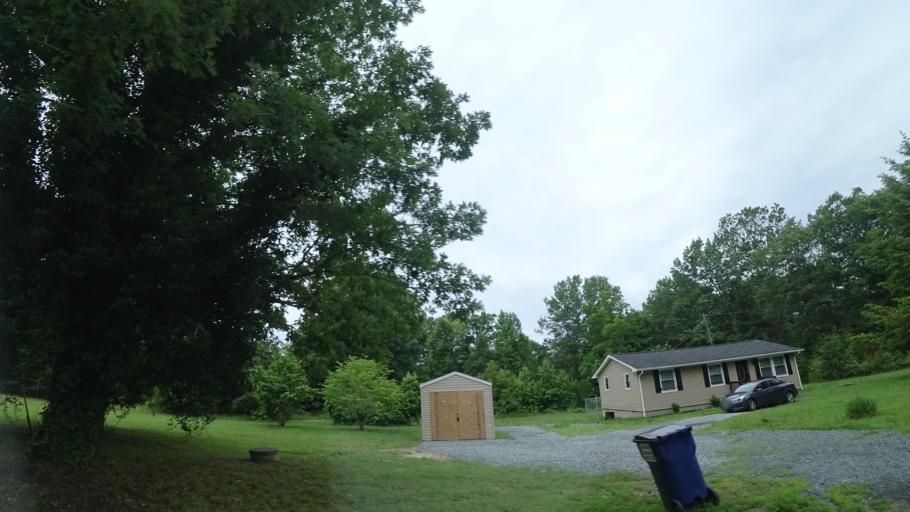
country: US
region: Virginia
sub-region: Spotsylvania County
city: Spotsylvania
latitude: 38.1263
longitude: -77.7778
